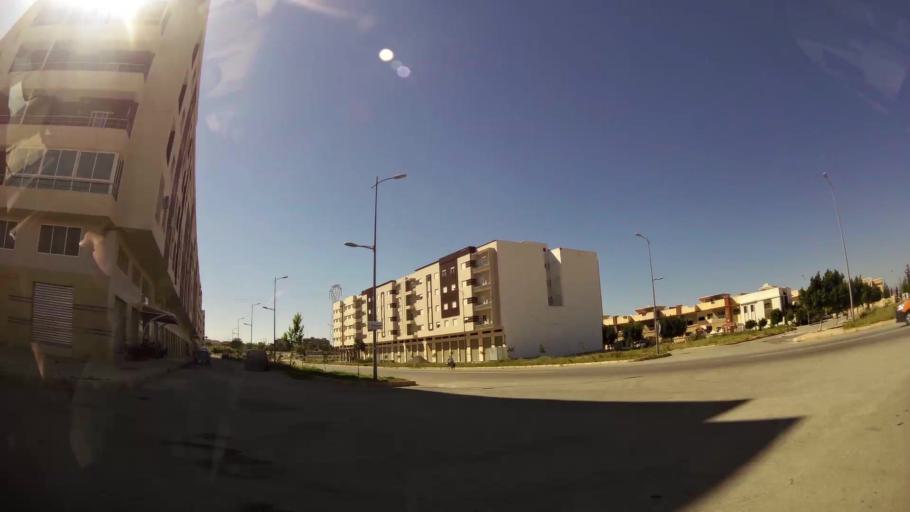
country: MA
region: Oriental
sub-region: Oujda-Angad
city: Oujda
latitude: 34.7222
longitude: -1.9084
